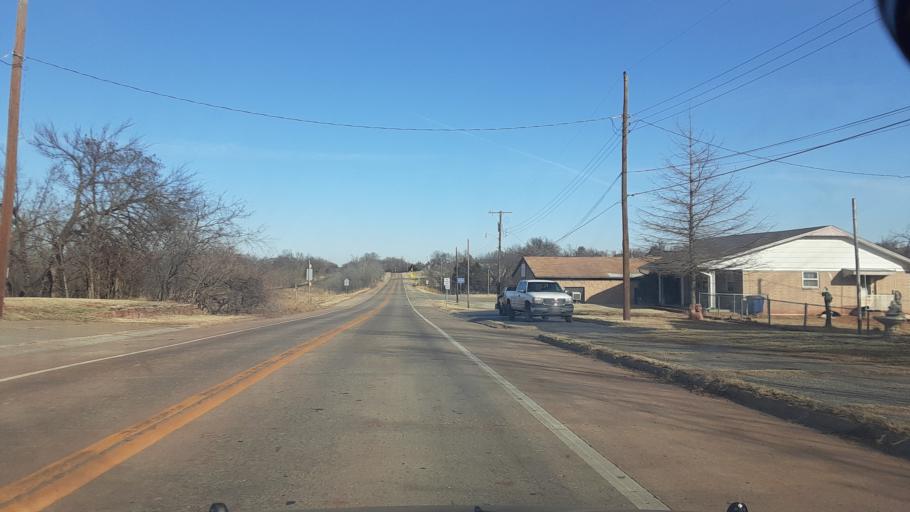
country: US
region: Oklahoma
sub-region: Logan County
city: Guthrie
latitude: 35.8875
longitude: -97.4240
